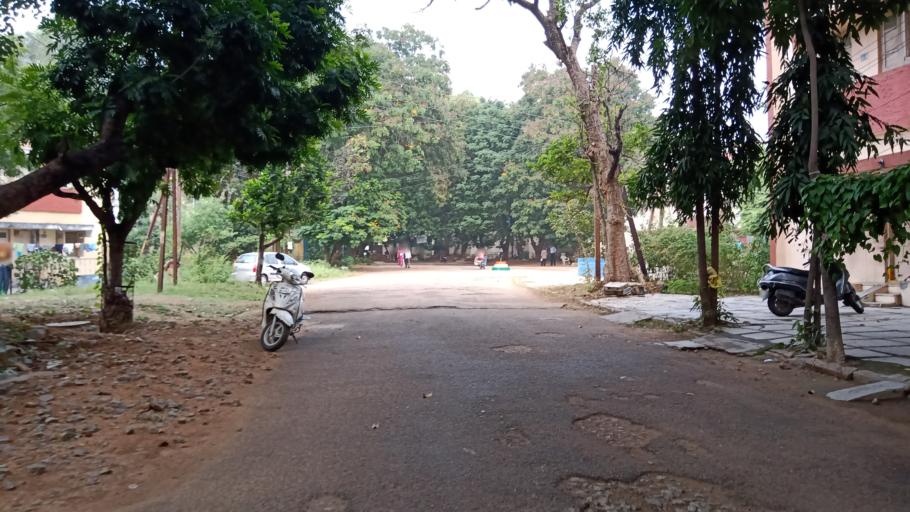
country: IN
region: Telangana
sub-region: Rangareddi
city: Kukatpalli
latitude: 17.4450
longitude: 78.4424
